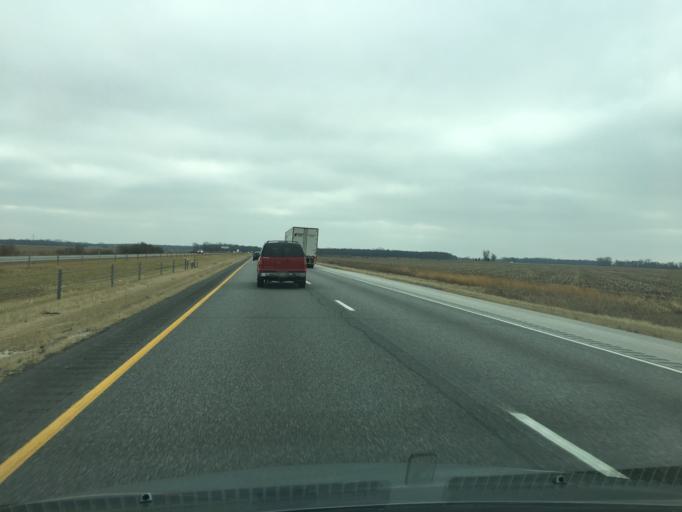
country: US
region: Indiana
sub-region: Jasper County
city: Rensselaer
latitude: 40.8583
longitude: -87.1842
